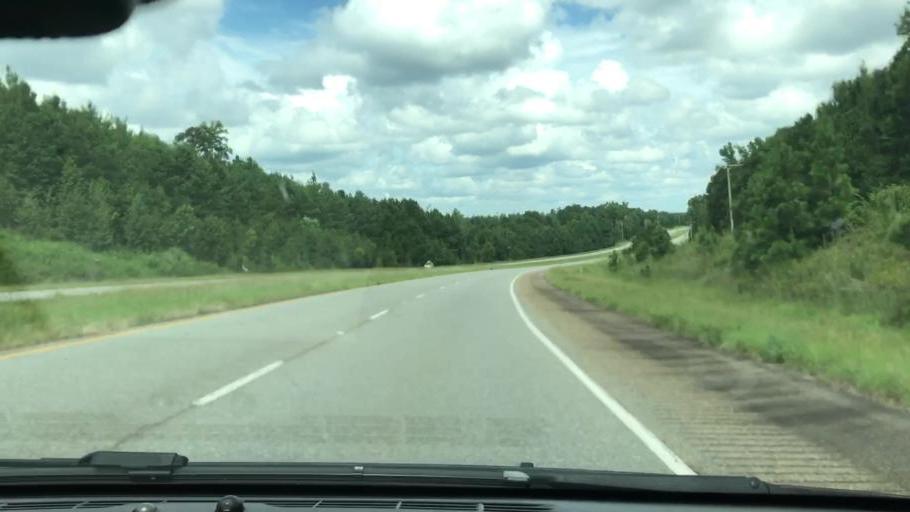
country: US
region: Georgia
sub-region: Stewart County
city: Lumpkin
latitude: 32.1245
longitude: -84.8215
